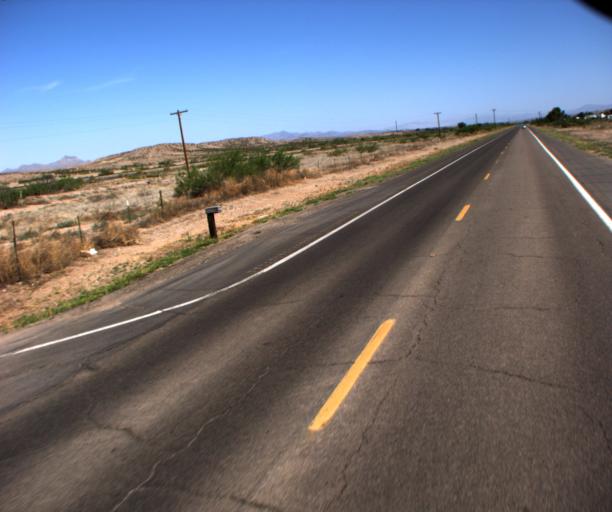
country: US
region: Arizona
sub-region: Greenlee County
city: Clifton
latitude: 32.6692
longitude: -109.0756
